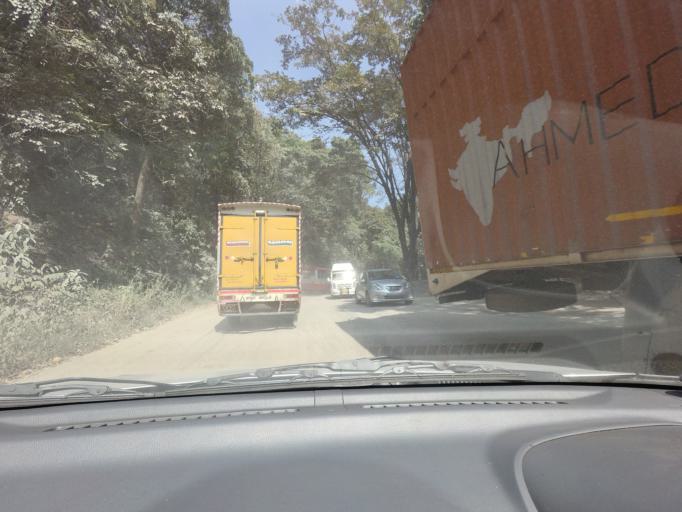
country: IN
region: Karnataka
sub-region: Hassan
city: Sakleshpur
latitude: 12.8306
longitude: 75.5938
